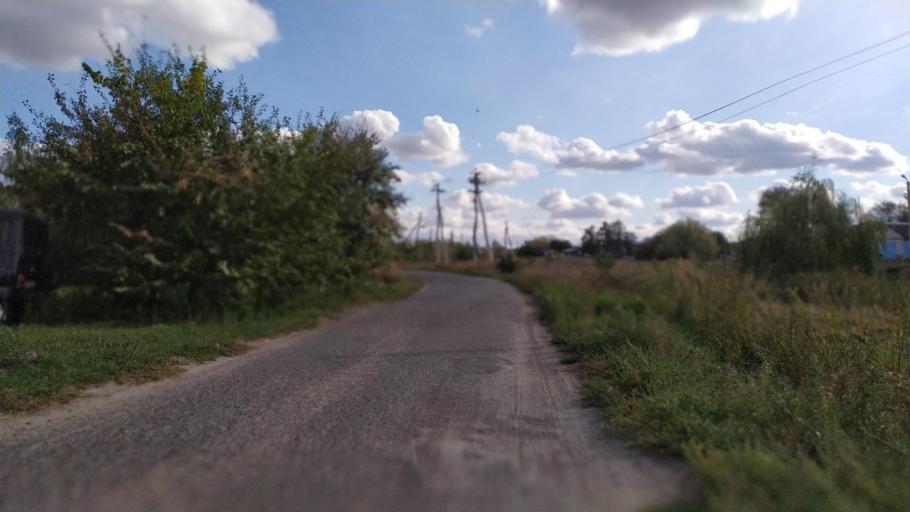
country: RU
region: Kursk
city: Kursk
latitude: 51.6355
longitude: 36.1502
